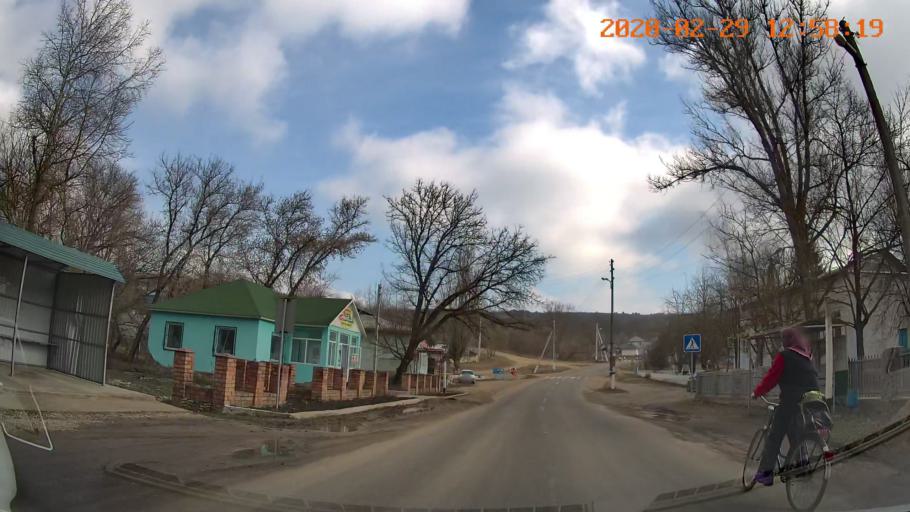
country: MD
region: Telenesti
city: Camenca
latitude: 48.0707
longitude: 28.7196
